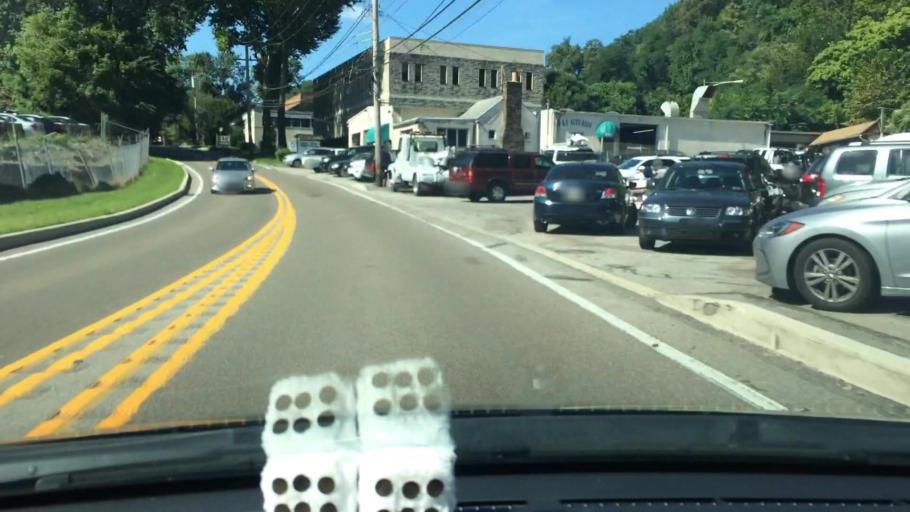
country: US
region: Pennsylvania
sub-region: Montgomery County
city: Bala-Cynwyd
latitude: 40.0205
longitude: -75.2376
